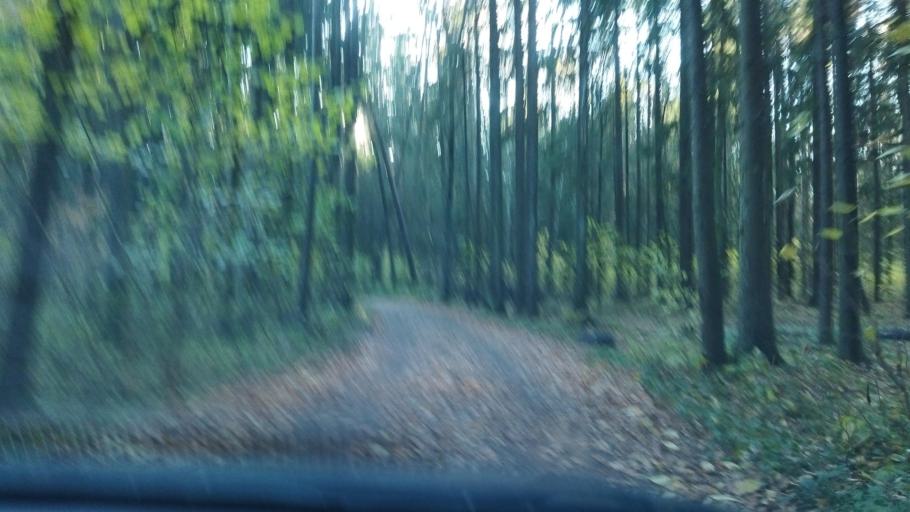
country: BY
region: Minsk
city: Slabada
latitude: 53.9856
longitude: 27.8888
